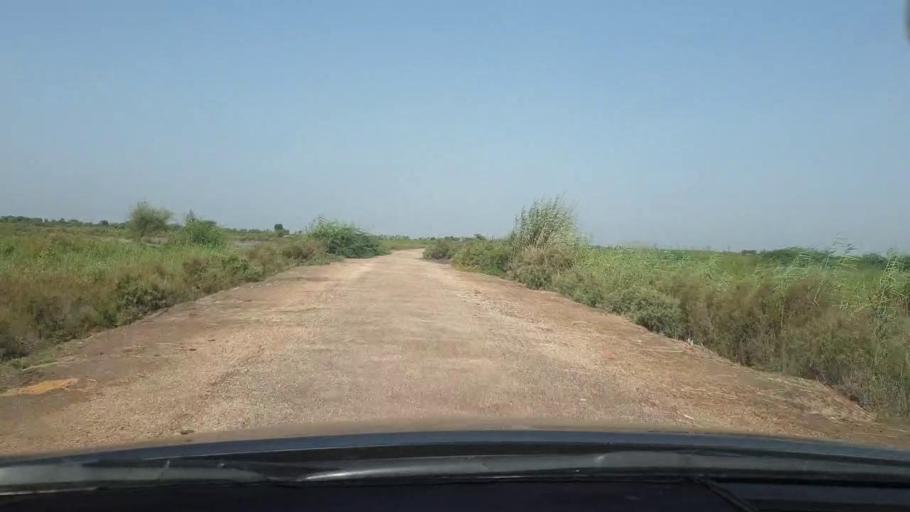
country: PK
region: Sindh
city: Tando Bago
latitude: 24.7099
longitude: 69.1093
